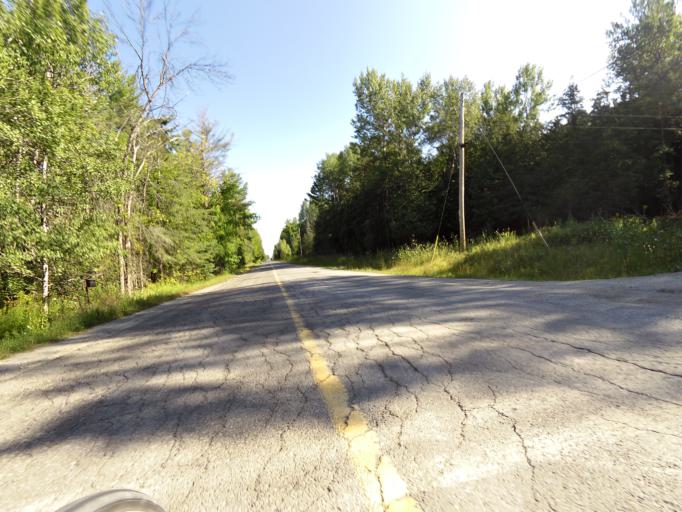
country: CA
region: Ontario
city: Bells Corners
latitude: 45.4744
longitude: -76.0176
